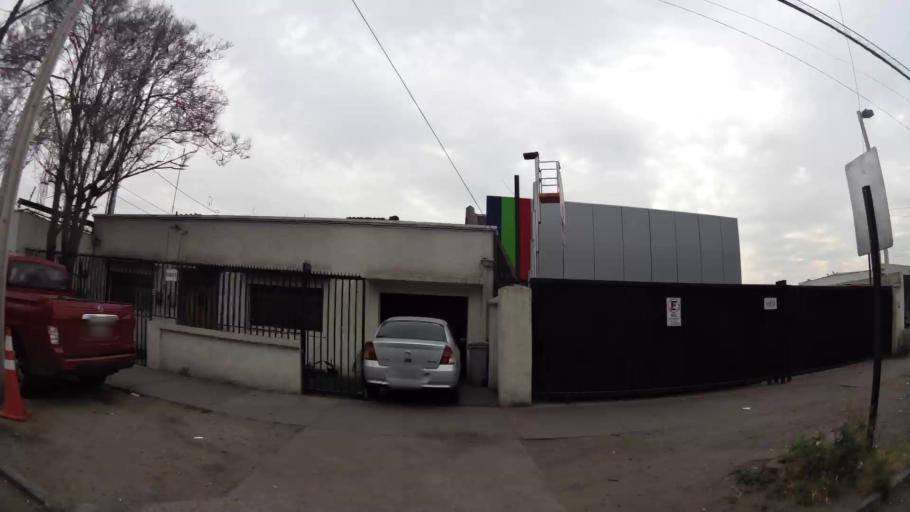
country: CL
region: Santiago Metropolitan
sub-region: Provincia de Santiago
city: Villa Presidente Frei, Nunoa, Santiago, Chile
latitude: -33.4749
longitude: -70.6063
